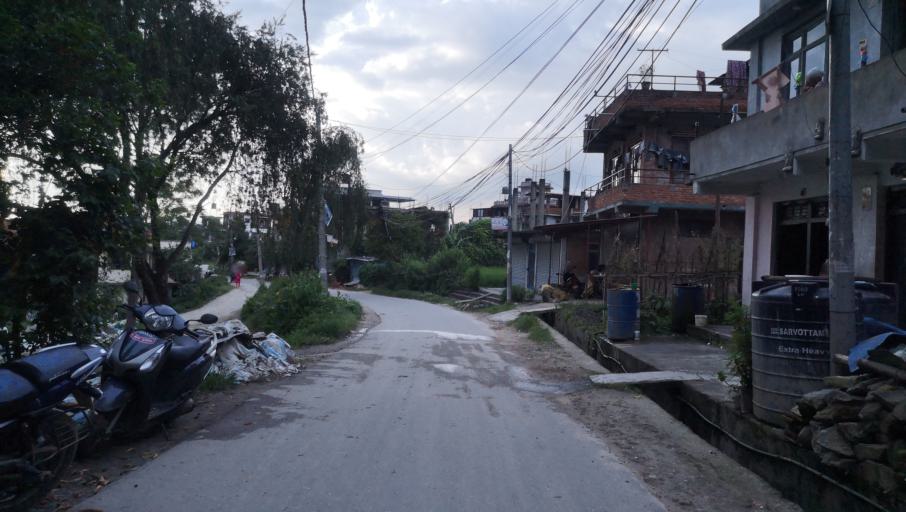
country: NP
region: Central Region
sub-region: Bagmati Zone
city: Bhaktapur
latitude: 27.6490
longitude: 85.3857
